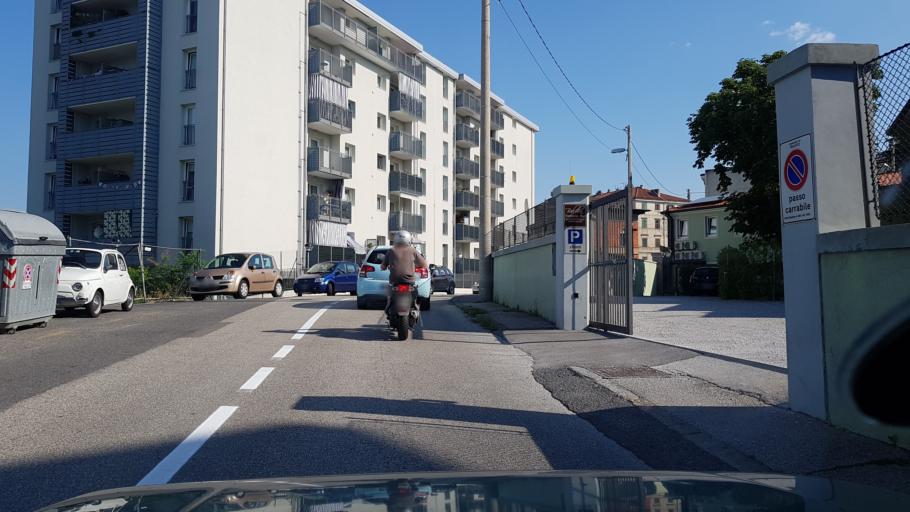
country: IT
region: Friuli Venezia Giulia
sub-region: Provincia di Trieste
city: Trieste
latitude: 45.6363
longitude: 13.7874
